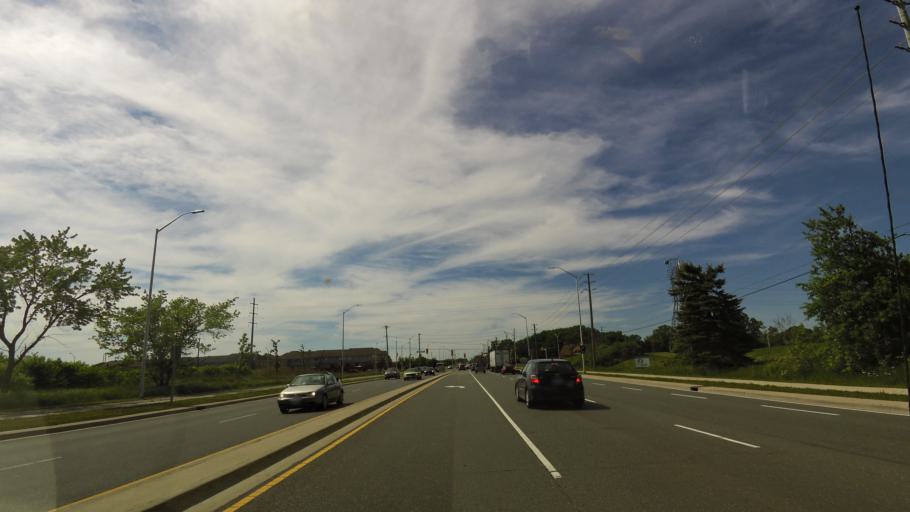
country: CA
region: Ontario
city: Oakville
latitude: 43.4219
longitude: -79.7574
